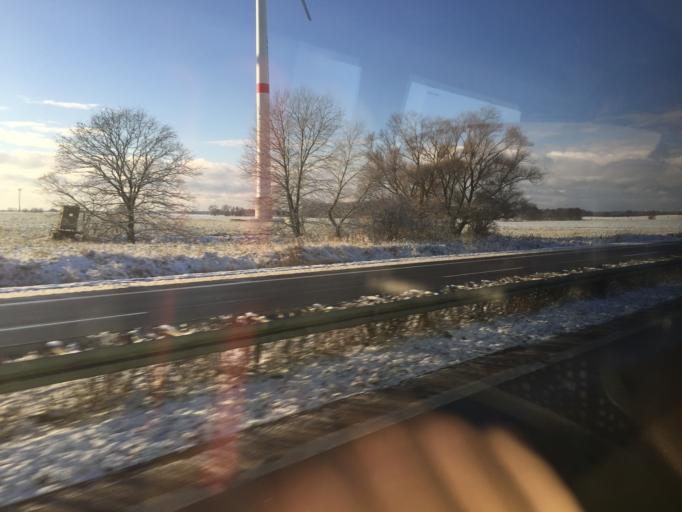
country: DE
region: Brandenburg
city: Heiligengrabe
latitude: 53.1855
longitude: 12.2904
